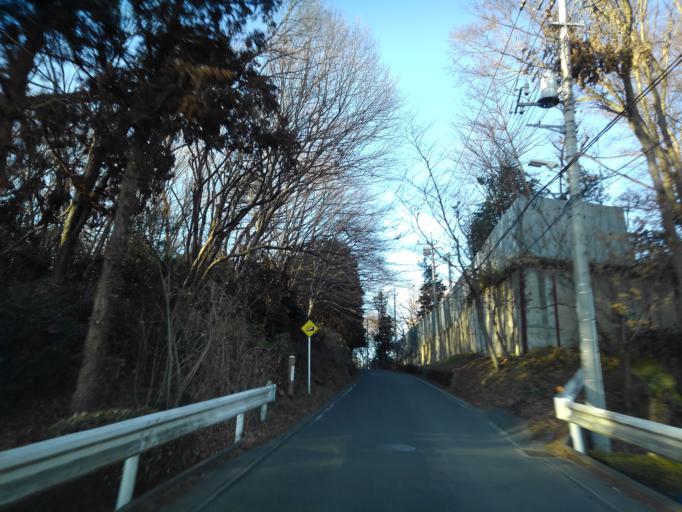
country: JP
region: Saitama
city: Sayama
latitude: 35.8080
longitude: 139.3835
